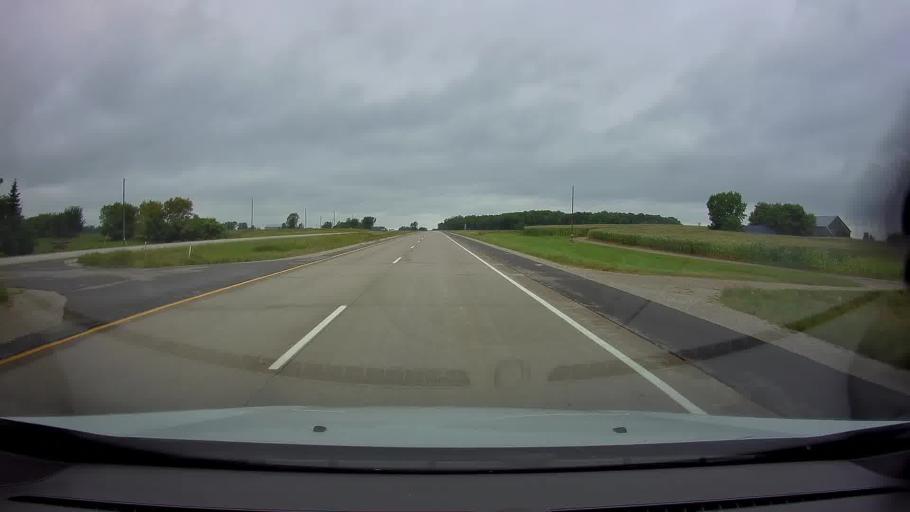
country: US
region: Wisconsin
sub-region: Brown County
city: Pulaski
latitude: 44.6245
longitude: -88.2729
